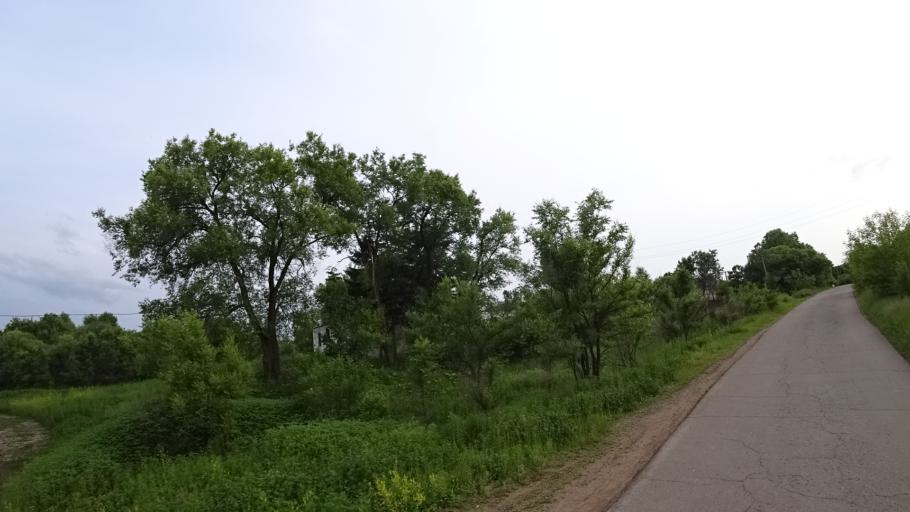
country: RU
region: Primorskiy
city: Novosysoyevka
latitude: 44.2450
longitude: 133.3695
